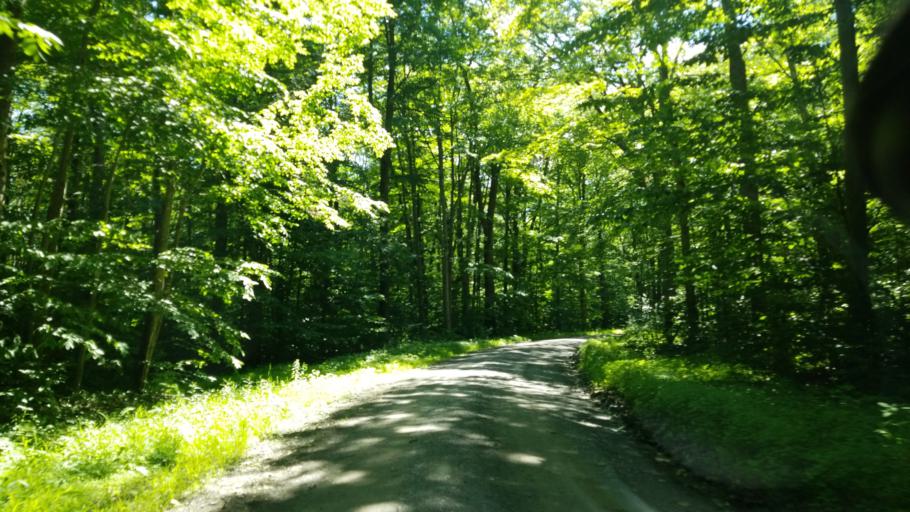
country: US
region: Pennsylvania
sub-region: Clearfield County
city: Clearfield
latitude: 41.2097
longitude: -78.4010
